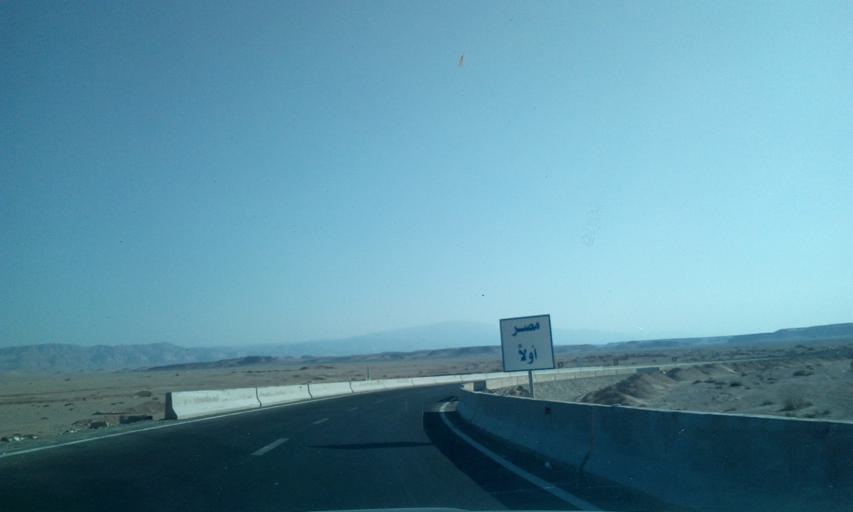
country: EG
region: As Suways
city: Ain Sukhna
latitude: 29.1066
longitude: 32.5338
